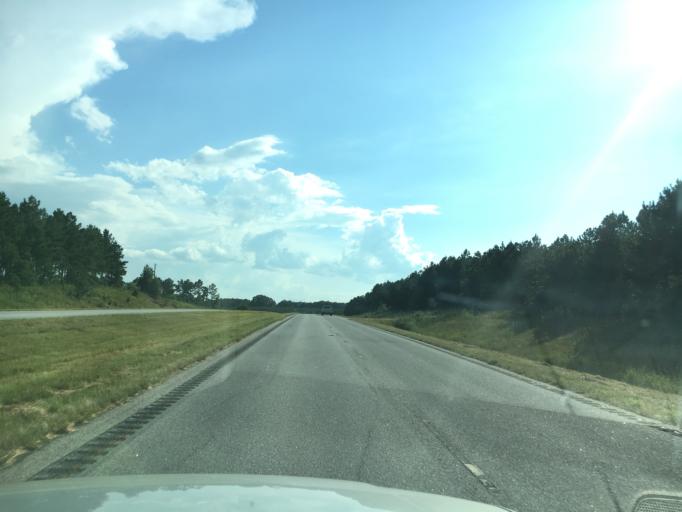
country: US
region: South Carolina
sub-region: Laurens County
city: Laurens
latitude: 34.3410
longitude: -81.9787
